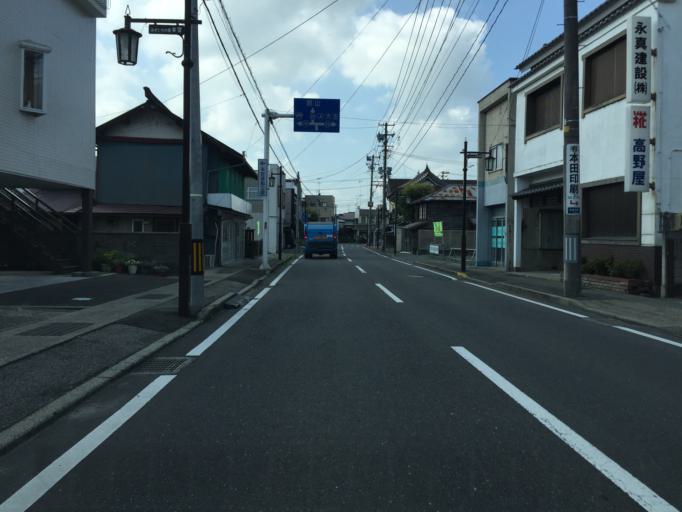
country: JP
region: Fukushima
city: Motomiya
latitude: 37.5191
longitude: 140.4048
